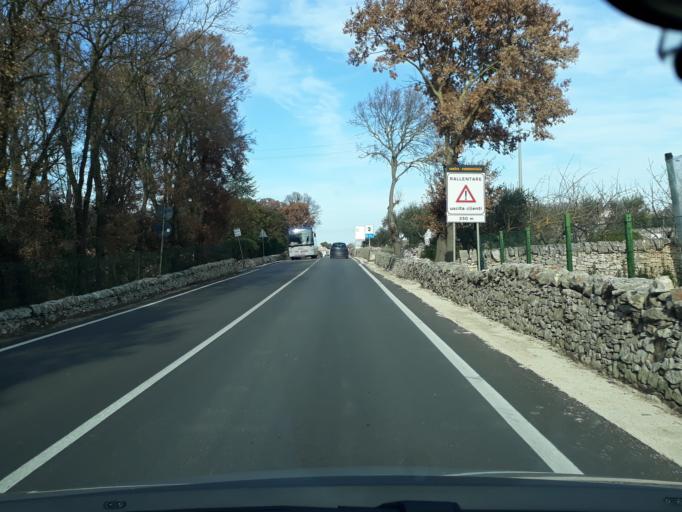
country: IT
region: Apulia
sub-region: Provincia di Bari
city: Locorotondo
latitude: 40.7720
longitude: 17.3346
